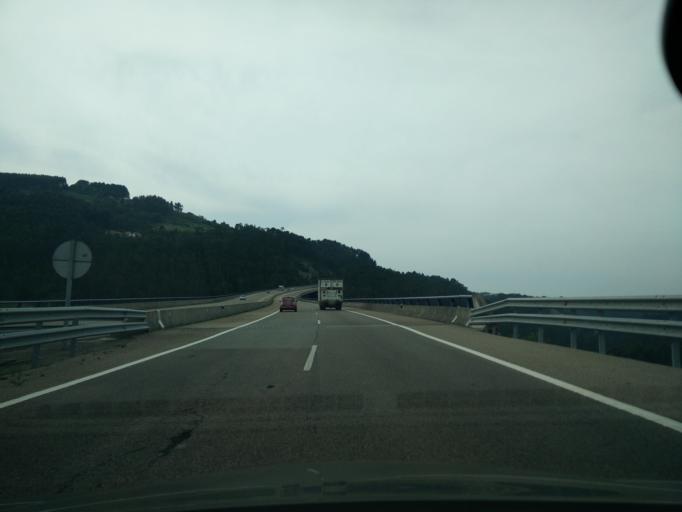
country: ES
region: Asturias
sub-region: Province of Asturias
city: Arriba
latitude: 43.4972
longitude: -5.5348
